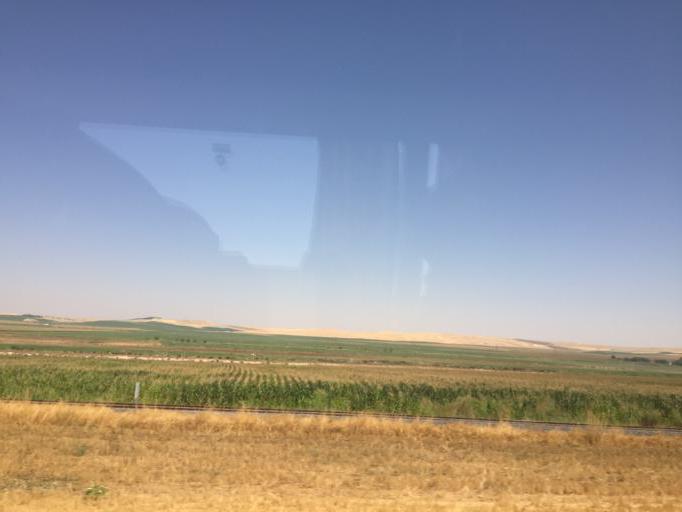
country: TR
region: Diyarbakir
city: Tepe
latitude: 37.8495
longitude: 40.7891
